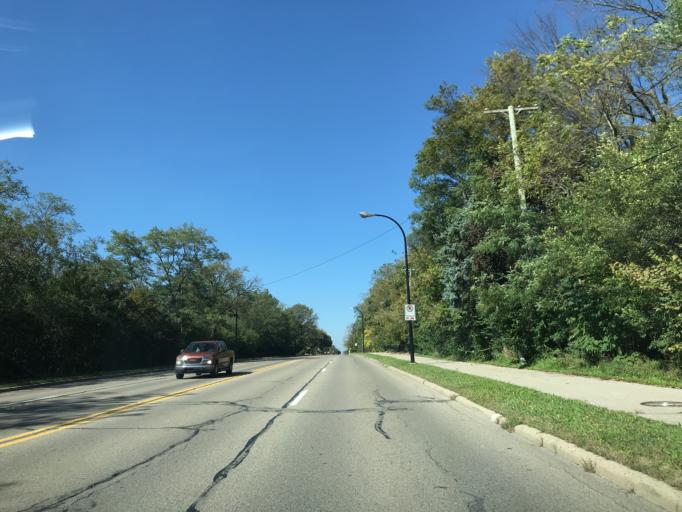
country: US
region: Michigan
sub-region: Washtenaw County
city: Ann Arbor
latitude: 42.2623
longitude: -83.7153
